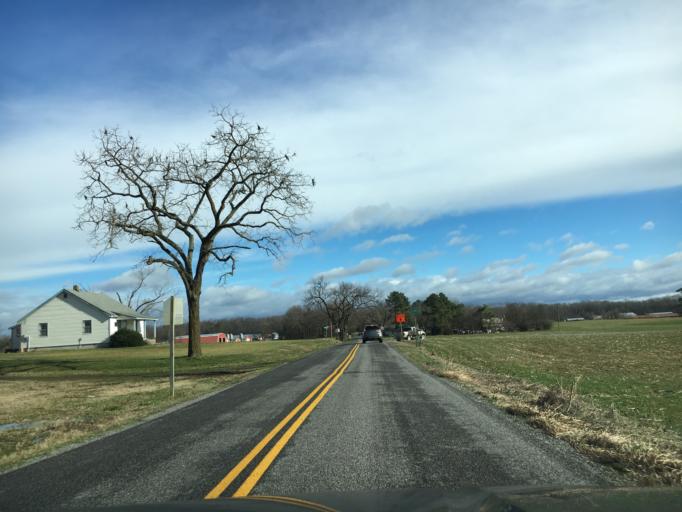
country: US
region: Virginia
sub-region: Amelia County
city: Amelia Court House
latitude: 37.4391
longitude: -78.0232
